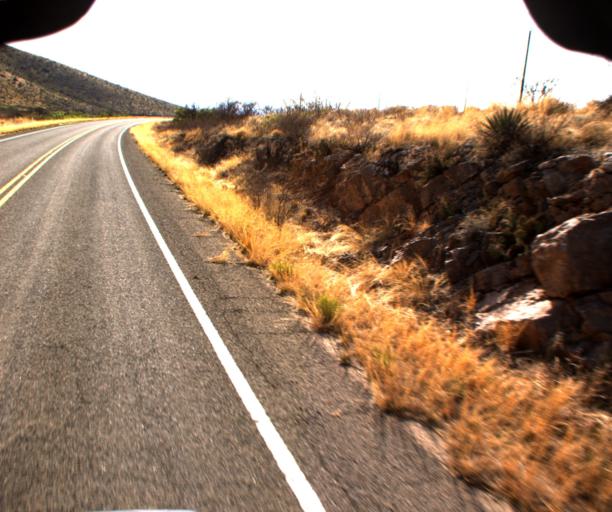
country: US
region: Arizona
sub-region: Cochise County
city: Willcox
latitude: 32.1829
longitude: -109.6540
